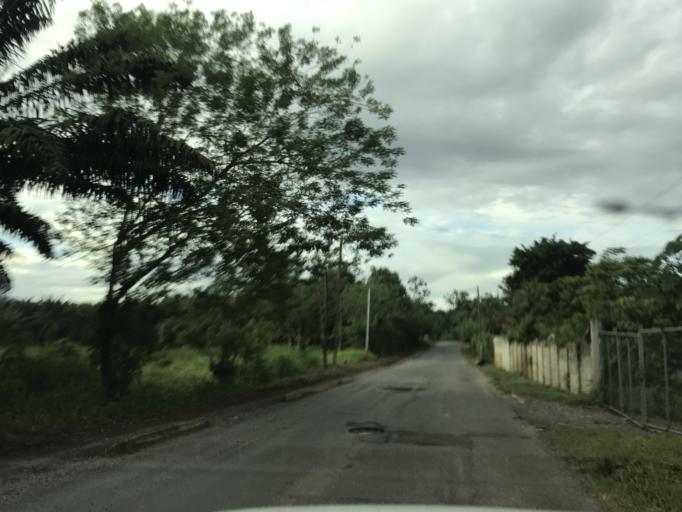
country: GT
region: Izabal
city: Morales
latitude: 15.6370
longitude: -89.0076
